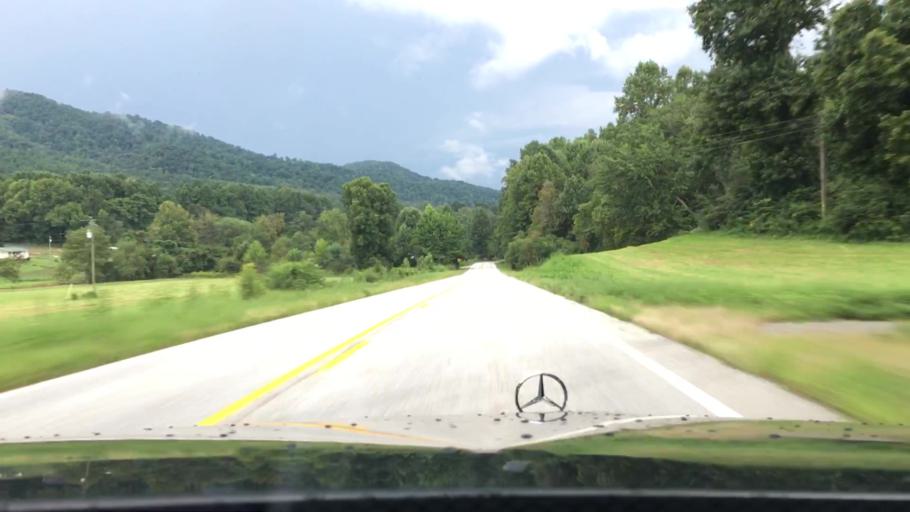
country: US
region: Virginia
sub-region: Nelson County
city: Lovingston
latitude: 37.8211
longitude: -78.9358
